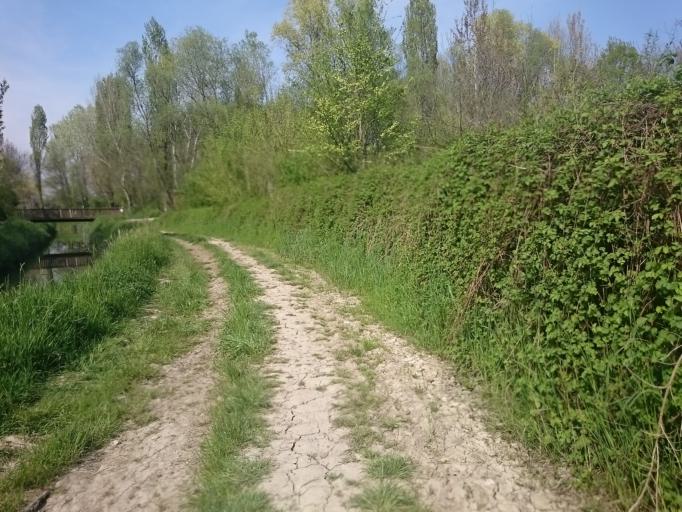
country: IT
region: Veneto
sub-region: Provincia di Padova
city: Bosco
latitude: 45.4367
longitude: 11.7878
